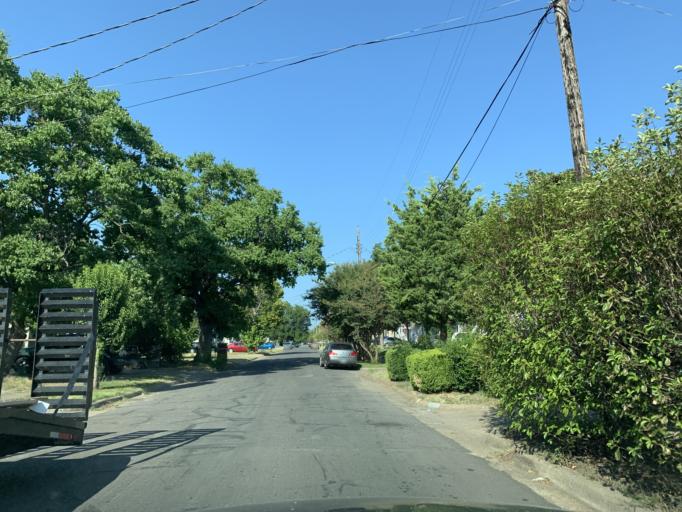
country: US
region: Texas
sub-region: Dallas County
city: Dallas
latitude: 32.7065
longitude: -96.7925
